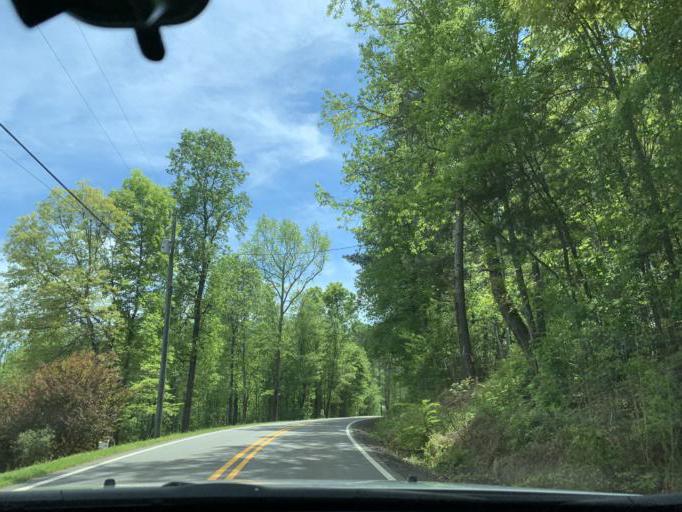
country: US
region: Georgia
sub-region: Hall County
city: Flowery Branch
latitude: 34.2718
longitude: -84.0238
